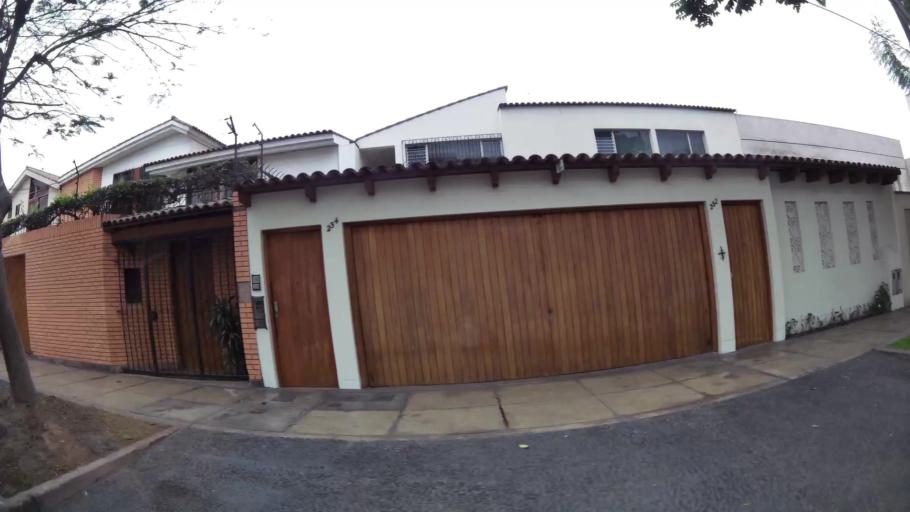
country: PE
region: Lima
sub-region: Lima
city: Surco
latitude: -12.1243
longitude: -77.0106
